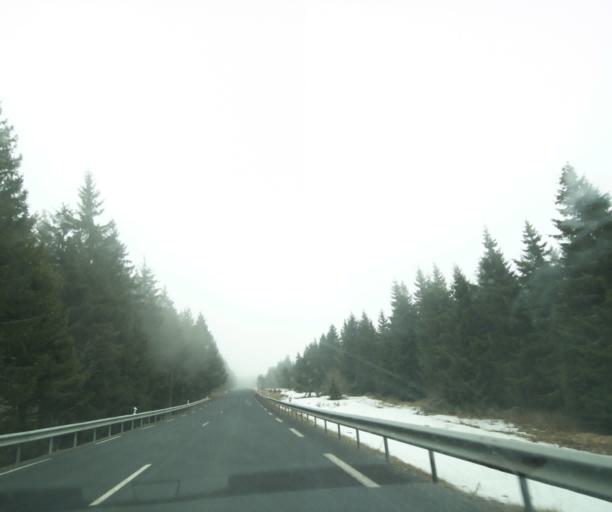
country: FR
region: Languedoc-Roussillon
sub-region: Departement de la Lozere
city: Langogne
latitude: 44.7525
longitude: 3.9444
